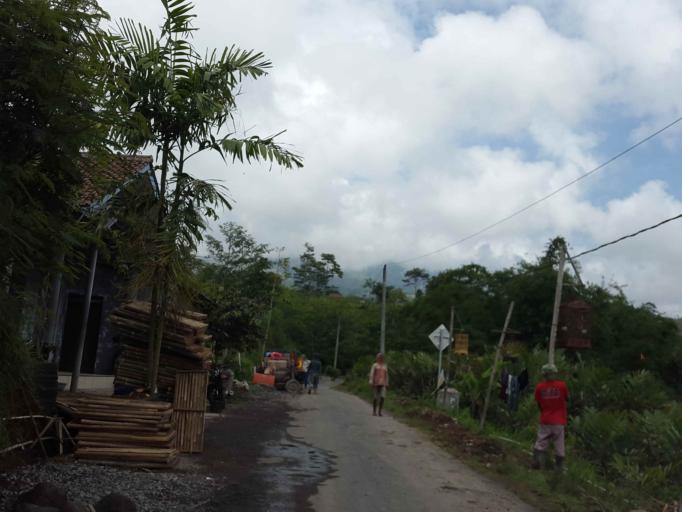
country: ID
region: Central Java
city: Magelang
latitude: -7.4458
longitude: 110.1264
